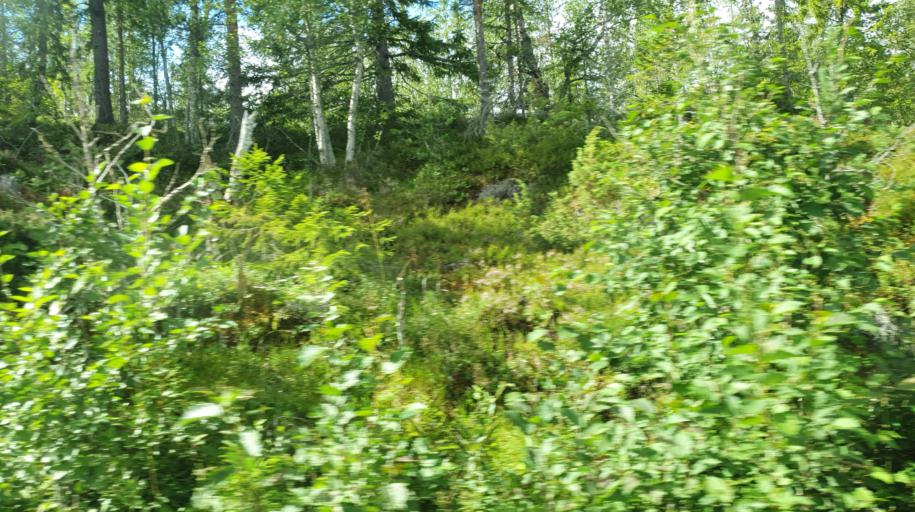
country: NO
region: Nord-Trondelag
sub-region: Levanger
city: Skogn
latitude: 63.5901
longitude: 11.2522
